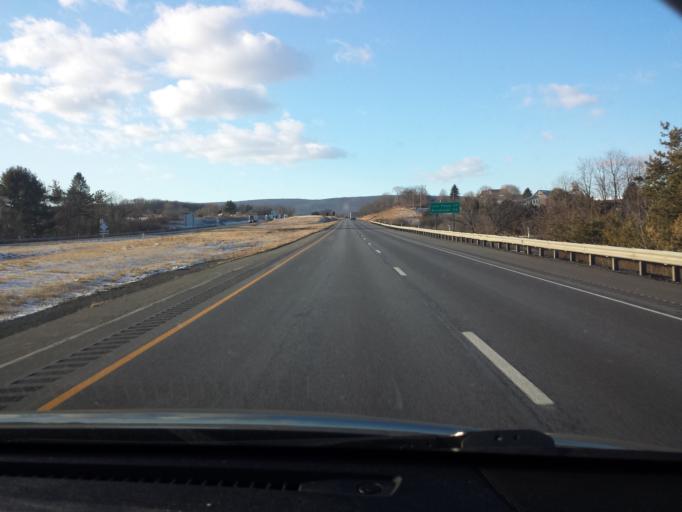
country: US
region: Pennsylvania
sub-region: Union County
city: New Columbia
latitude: 41.0562
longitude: -76.8862
